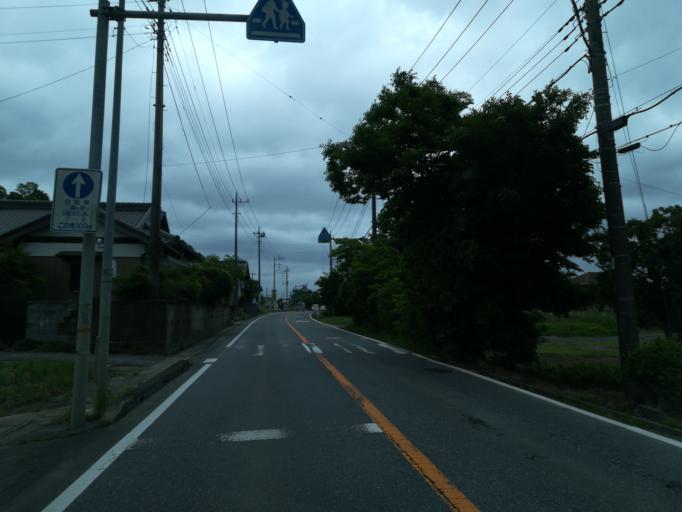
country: JP
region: Ibaraki
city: Tsukuba
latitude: 36.1890
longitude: 140.0792
